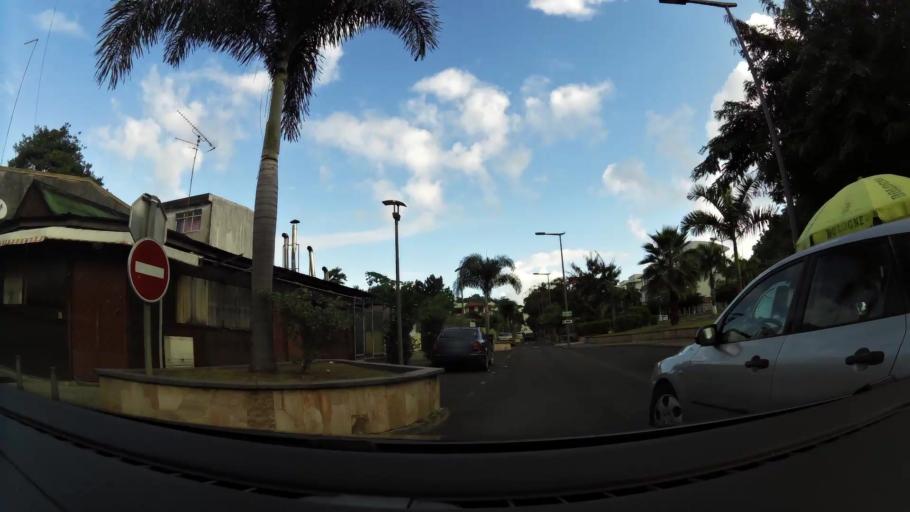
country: GP
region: Guadeloupe
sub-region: Guadeloupe
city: Pointe-a-Pitre
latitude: 16.2432
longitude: -61.5311
